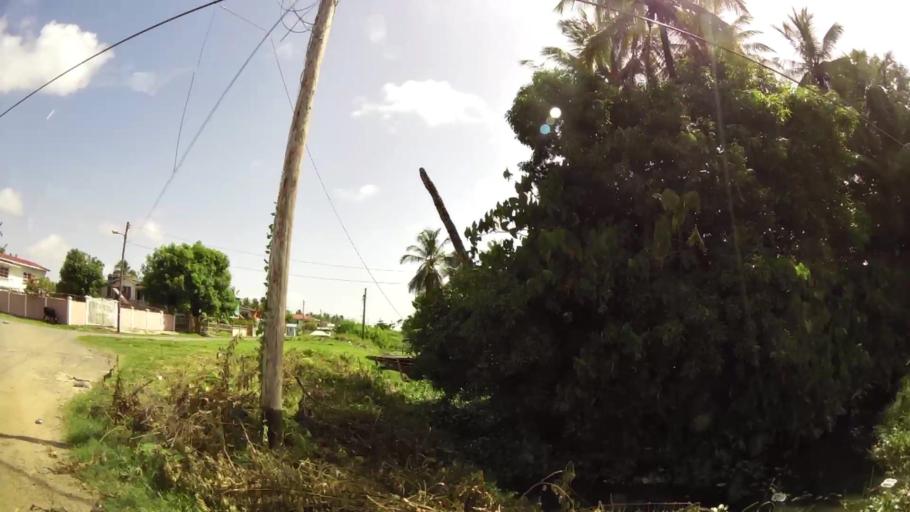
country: GY
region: Demerara-Mahaica
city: Mahaica Village
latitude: 6.7520
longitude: -57.9942
